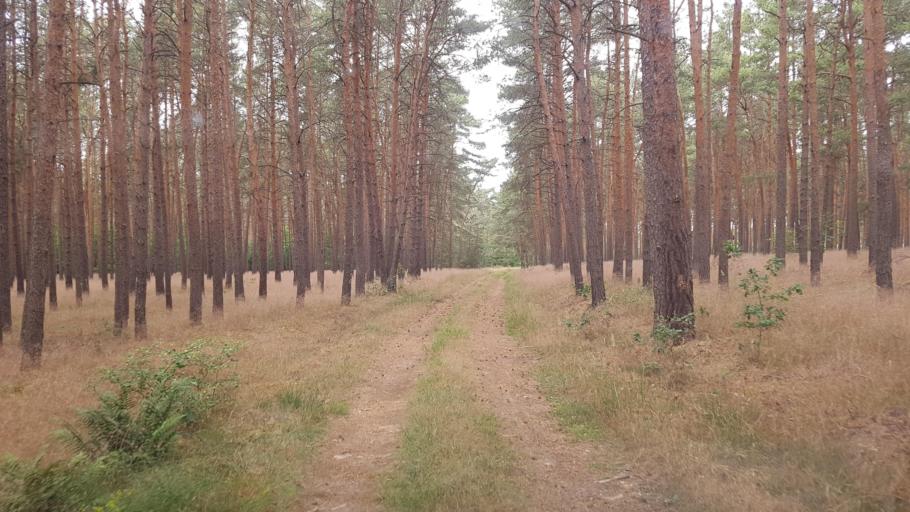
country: DE
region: Brandenburg
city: Treuenbrietzen
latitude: 52.0445
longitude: 12.8230
